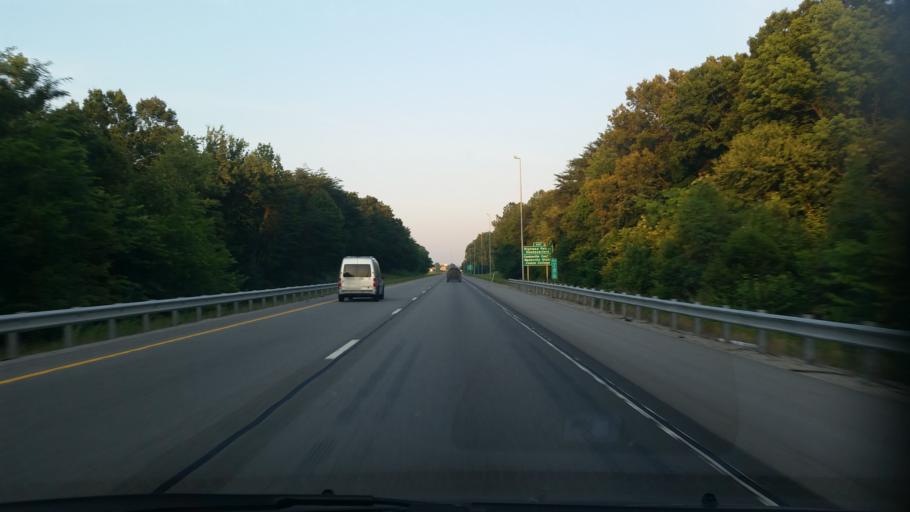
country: US
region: Tennessee
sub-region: Putnam County
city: Cookeville
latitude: 36.1362
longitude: -85.5247
